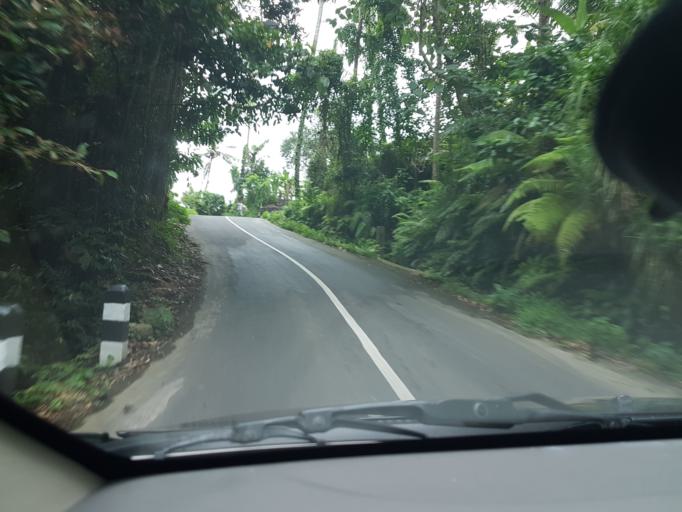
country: ID
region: Bali
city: Banjar Triwangsakeliki
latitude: -8.4573
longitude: 115.2753
